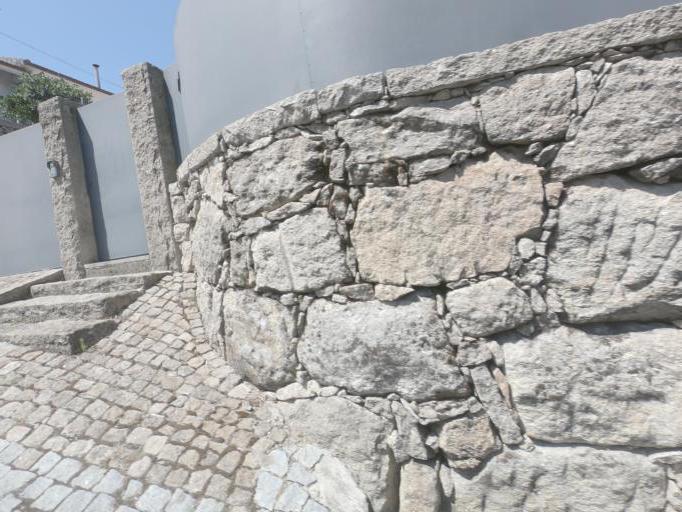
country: PT
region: Porto
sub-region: Amarante
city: Amarante
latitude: 41.2651
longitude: -8.0945
